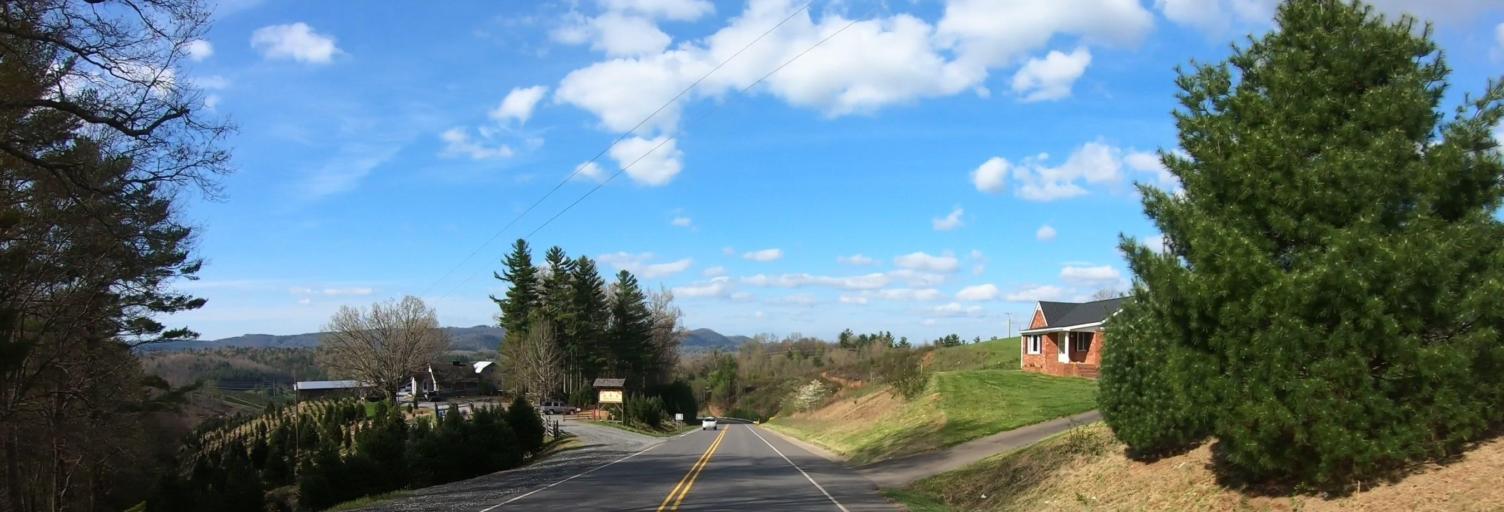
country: US
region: North Carolina
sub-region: Ashe County
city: Jefferson
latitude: 36.3429
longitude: -81.3829
